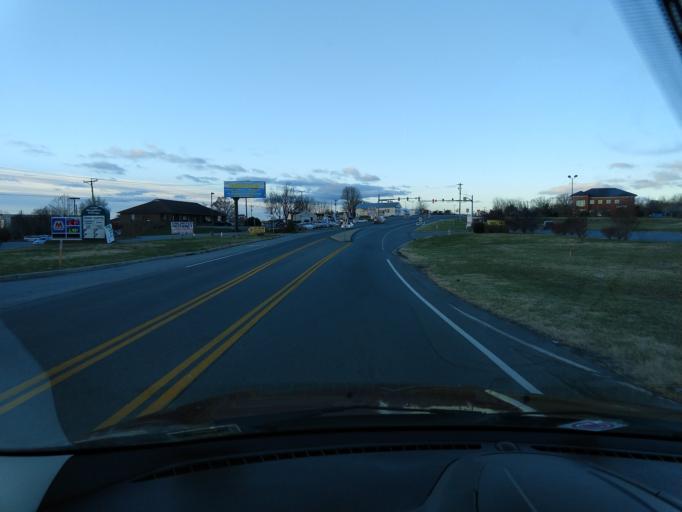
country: US
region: Virginia
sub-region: Franklin County
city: North Shore
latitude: 37.1668
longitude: -79.6353
